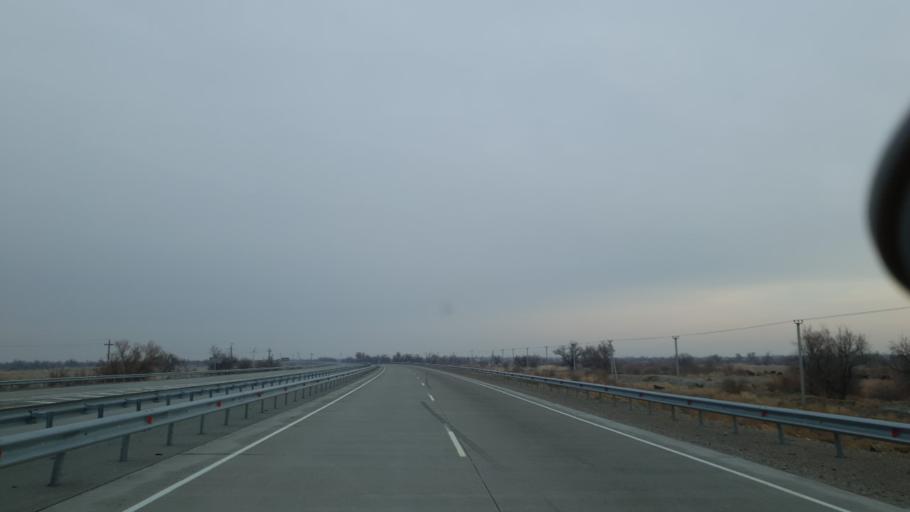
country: KZ
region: Almaty Oblysy
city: Zharkent
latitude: 43.9882
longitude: 79.6395
